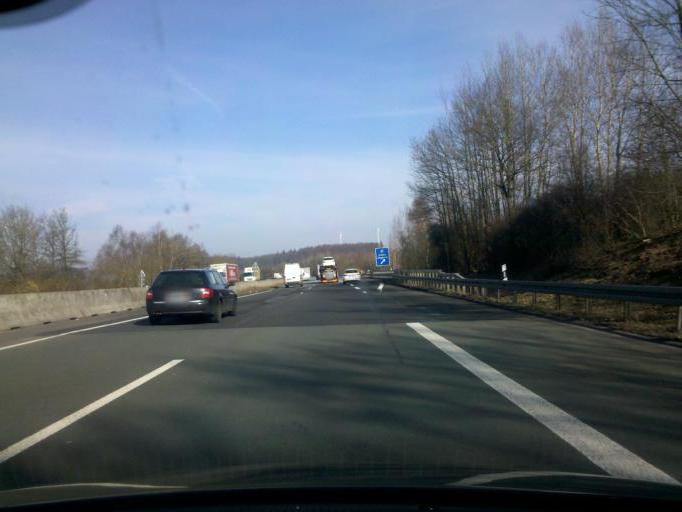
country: DE
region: North Rhine-Westphalia
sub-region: Regierungsbezirk Arnsberg
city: Wenden
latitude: 50.9408
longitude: 7.8784
